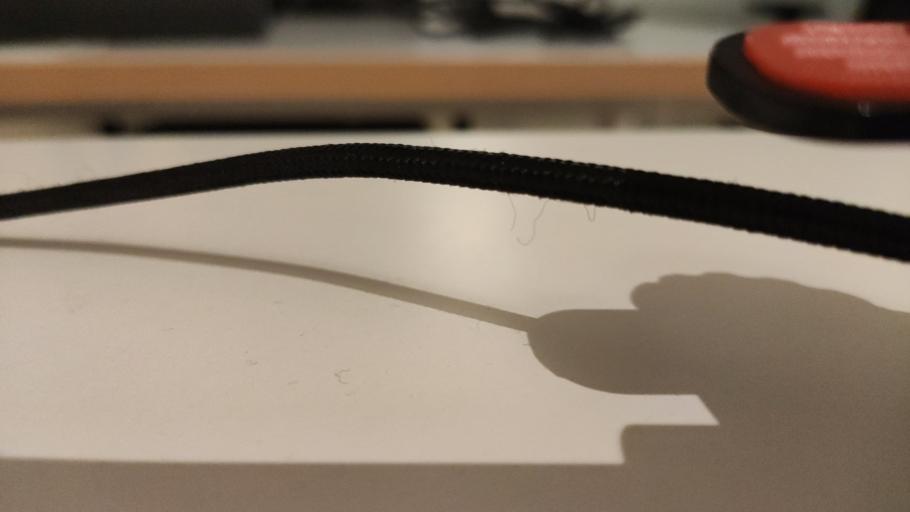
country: RU
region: Moskovskaya
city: Kurovskoye
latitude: 55.5832
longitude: 38.8902
